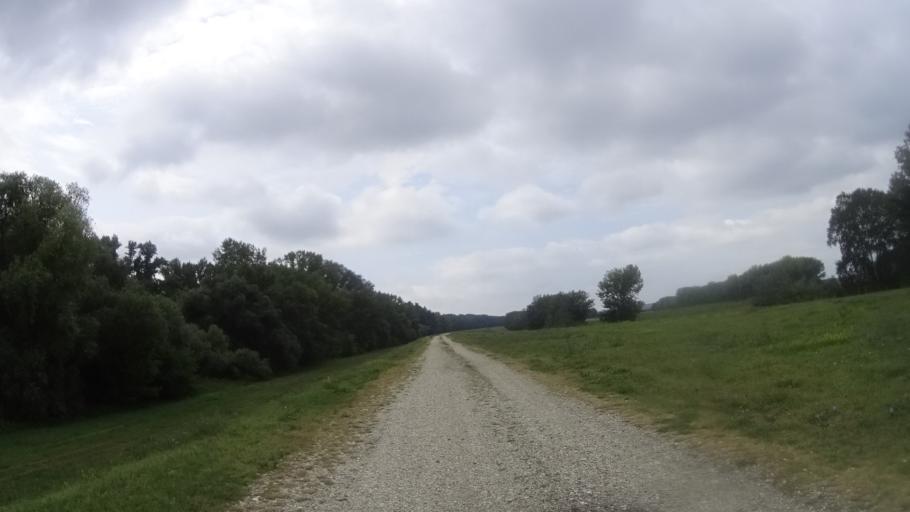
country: HU
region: Komarom-Esztergom
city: Acs
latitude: 47.7536
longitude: 17.9191
